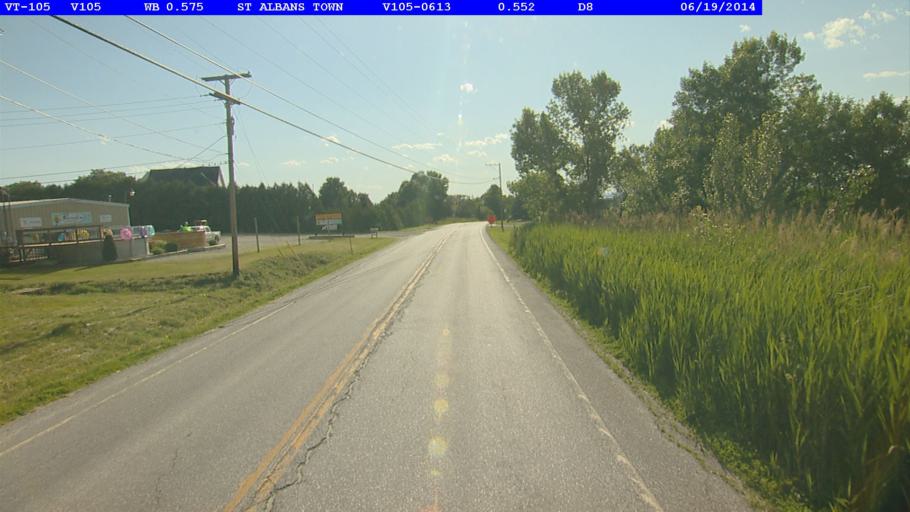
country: US
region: Vermont
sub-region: Franklin County
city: Saint Albans
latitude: 44.8271
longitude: -73.0717
